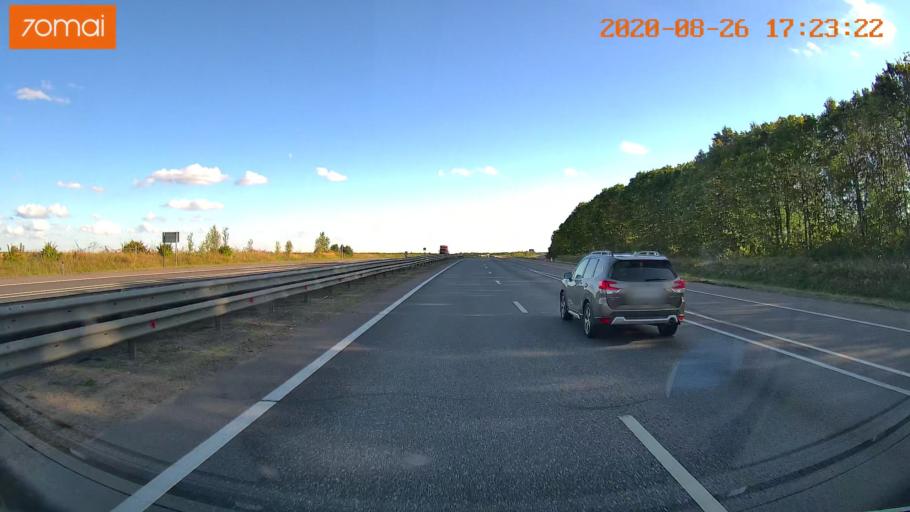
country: RU
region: Tula
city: Volovo
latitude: 53.5354
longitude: 38.1189
